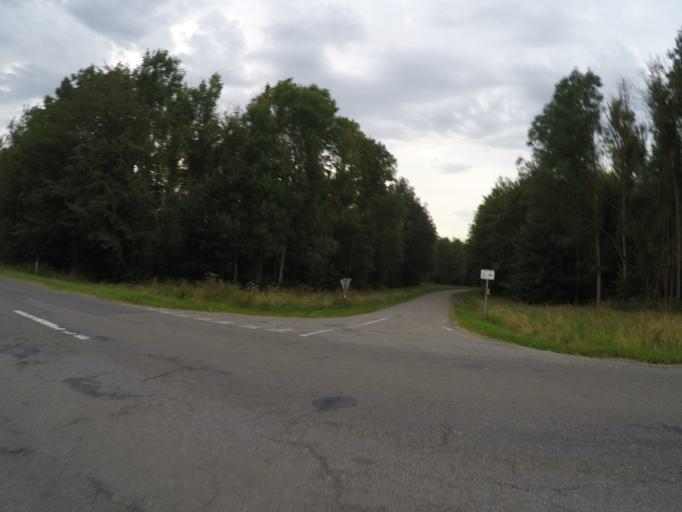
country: BE
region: Wallonia
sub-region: Province de Namur
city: Assesse
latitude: 50.3142
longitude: 5.0373
